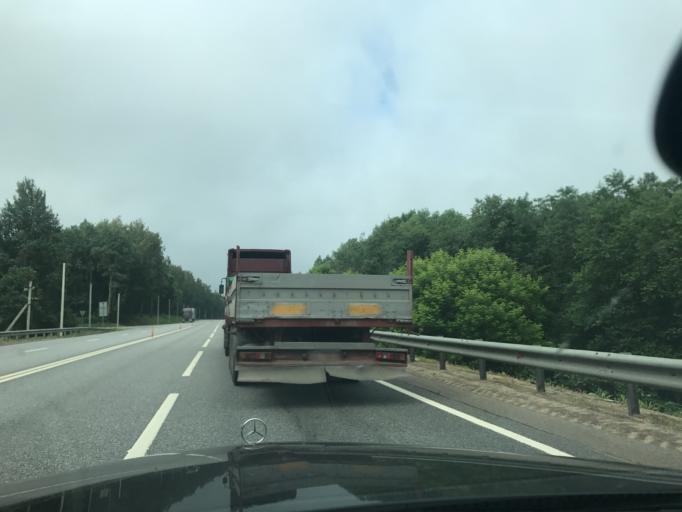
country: RU
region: Smolensk
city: Pechersk
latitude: 54.8918
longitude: 32.1059
